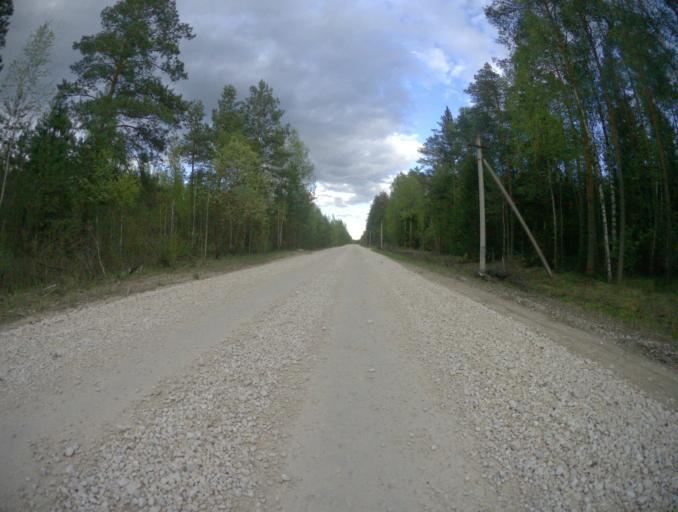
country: RU
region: Vladimir
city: Gusevskiy
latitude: 55.7208
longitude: 40.5860
